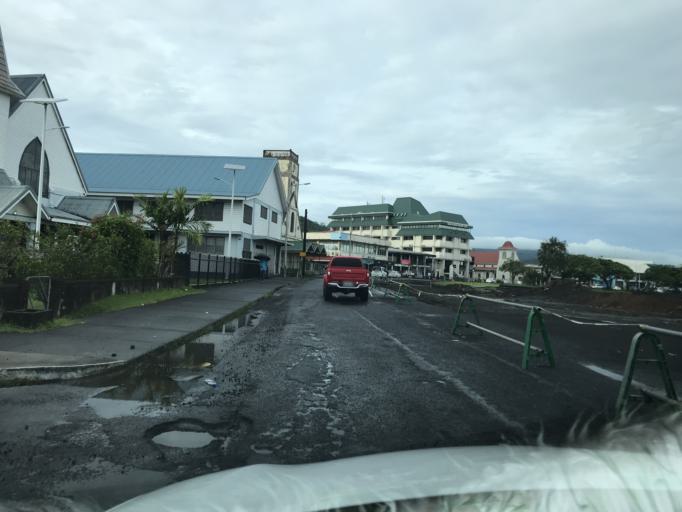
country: WS
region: Tuamasaga
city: Apia
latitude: -13.8325
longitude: -171.7609
